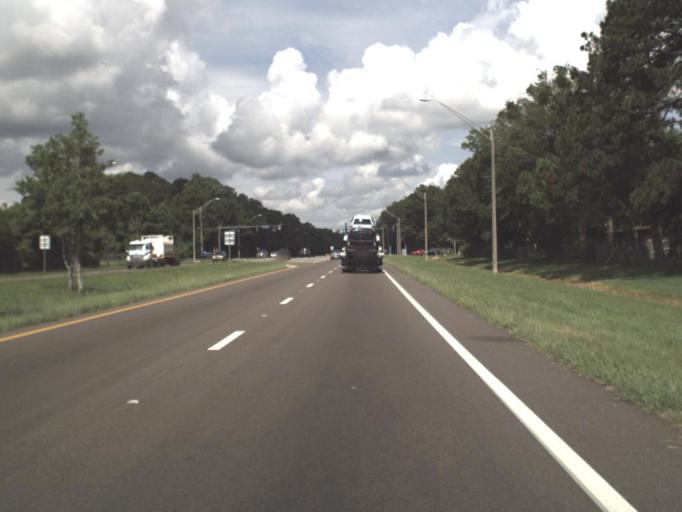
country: US
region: Florida
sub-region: Duval County
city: Jacksonville
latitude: 30.3569
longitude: -81.6991
